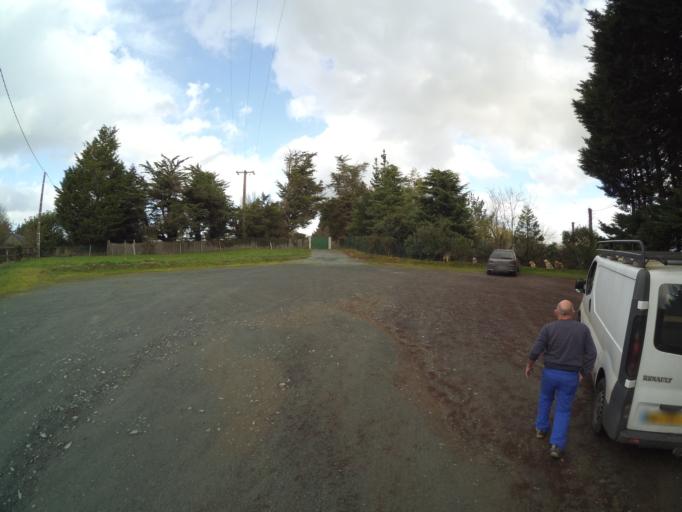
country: FR
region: Pays de la Loire
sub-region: Departement de la Loire-Atlantique
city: Bouvron
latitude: 47.4750
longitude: -1.8399
